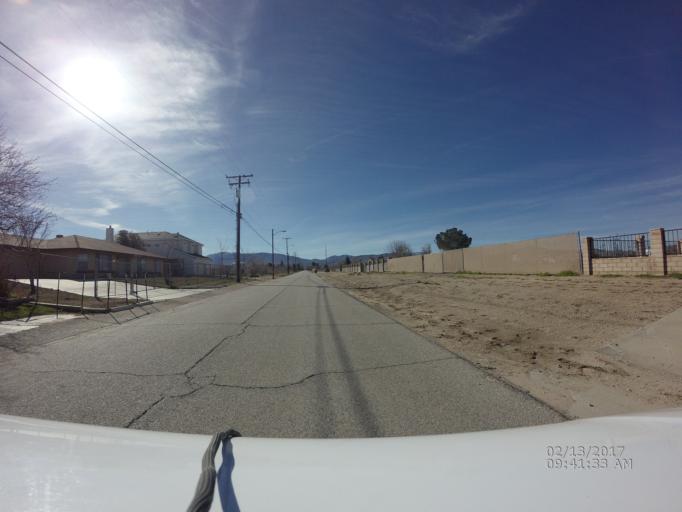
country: US
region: California
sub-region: Los Angeles County
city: Littlerock
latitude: 34.5524
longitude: -117.9670
